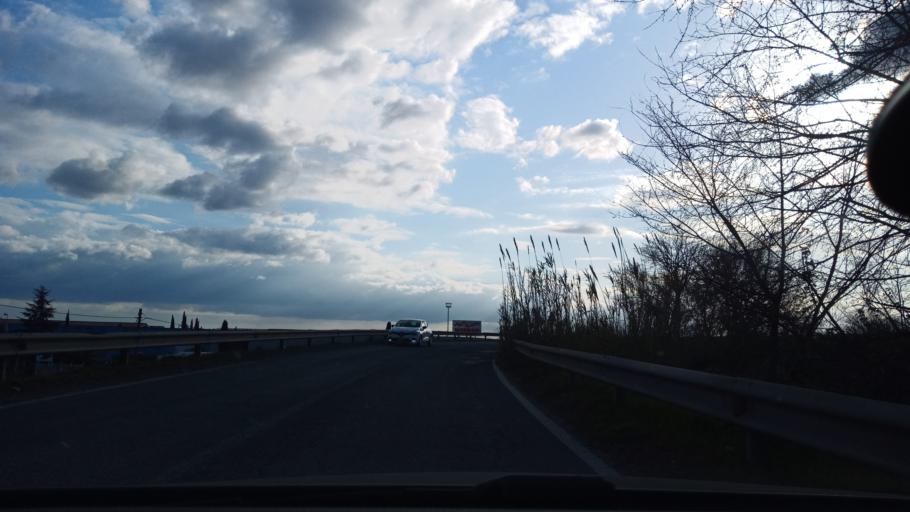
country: IT
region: Latium
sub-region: Citta metropolitana di Roma Capitale
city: Fiano Romano
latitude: 42.1475
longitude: 12.6221
